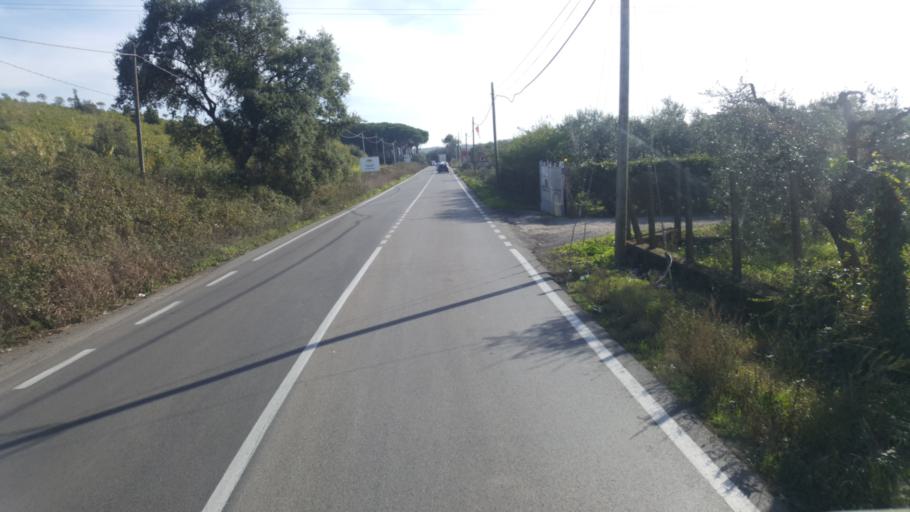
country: IT
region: Latium
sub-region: Citta metropolitana di Roma Capitale
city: Mantiglia di Ardea
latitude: 41.6864
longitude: 12.6100
